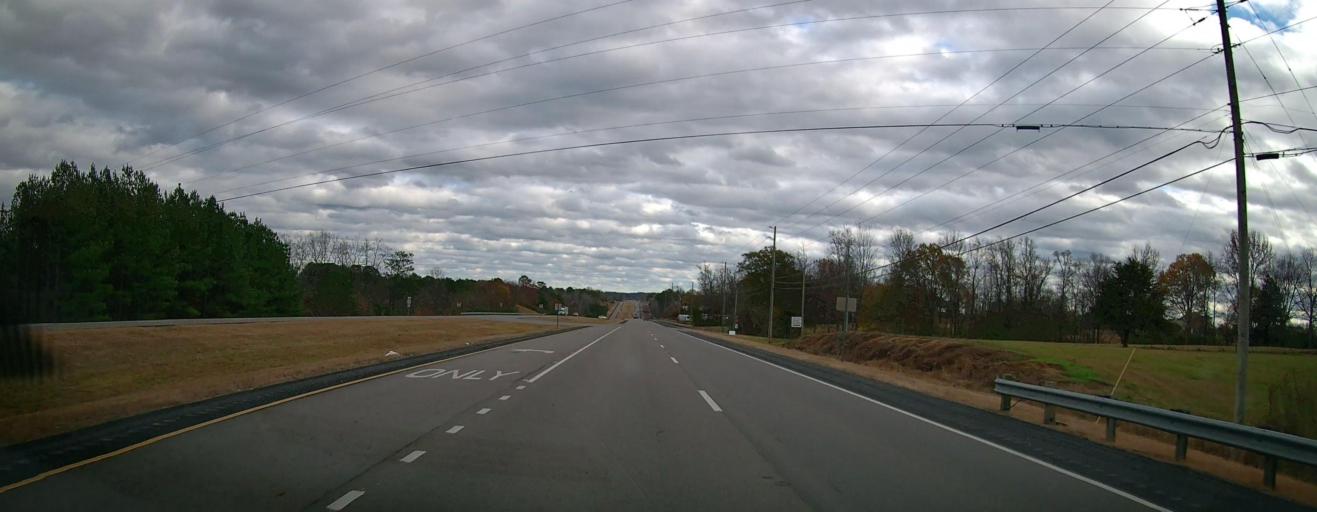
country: US
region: Alabama
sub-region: Morgan County
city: Falkville
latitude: 34.2620
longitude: -86.9861
